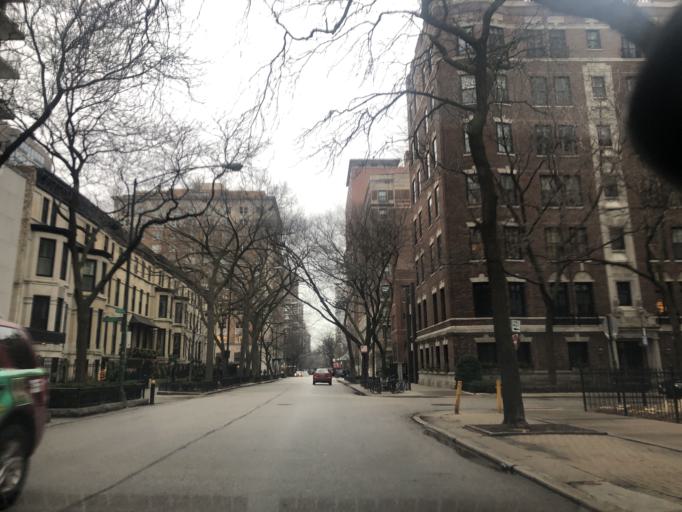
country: US
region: Illinois
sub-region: Cook County
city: Chicago
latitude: 41.9045
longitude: -87.6287
